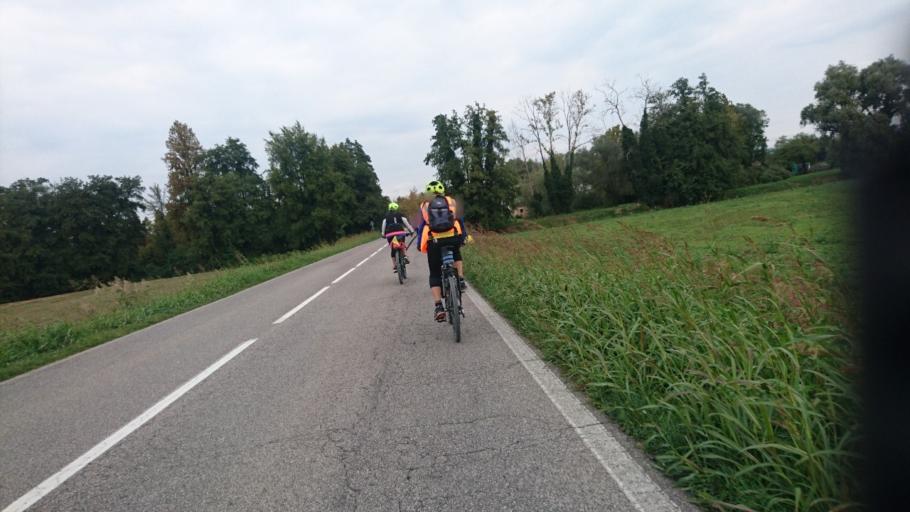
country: IT
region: Veneto
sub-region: Provincia di Verona
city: Zevio
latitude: 45.4018
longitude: 11.1253
